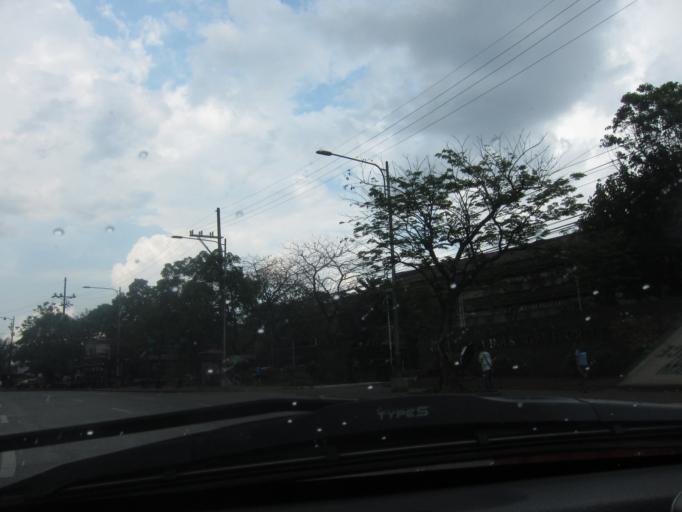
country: PH
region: Metro Manila
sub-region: Quezon City
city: Quezon City
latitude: 14.6495
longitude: 121.0518
